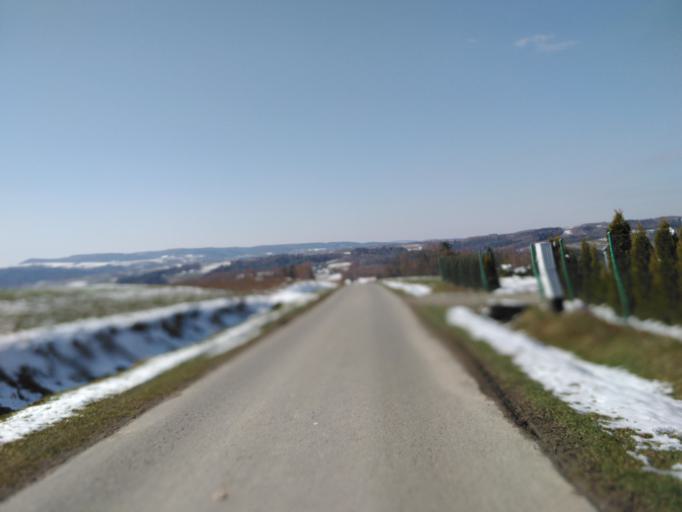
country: PL
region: Subcarpathian Voivodeship
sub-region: Powiat ropczycko-sedziszowski
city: Wielopole Skrzynskie
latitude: 49.9694
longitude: 21.5968
